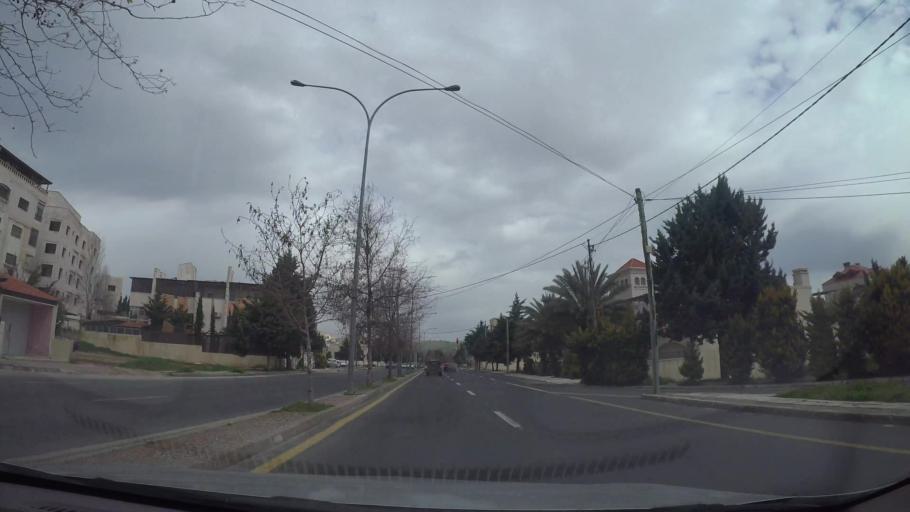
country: JO
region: Amman
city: Wadi as Sir
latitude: 31.9910
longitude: 35.8179
